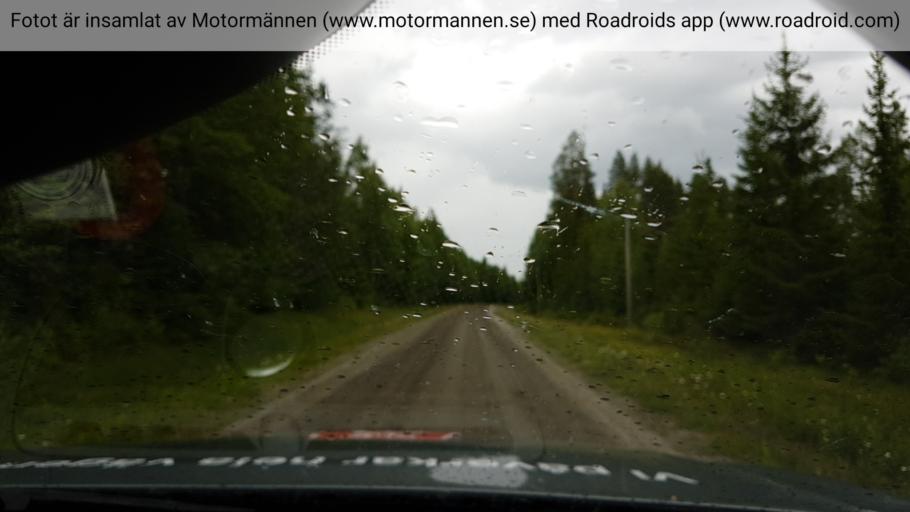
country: SE
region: Jaemtland
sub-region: Bergs Kommun
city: Hoverberg
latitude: 62.5211
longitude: 14.7082
